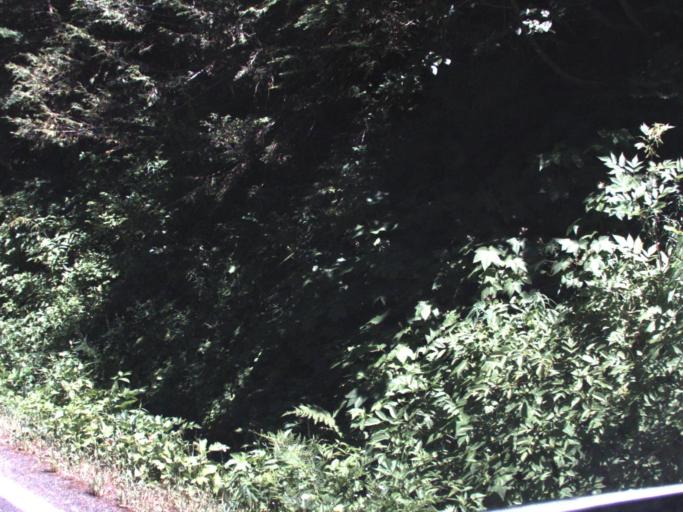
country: US
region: Washington
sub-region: King County
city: Enumclaw
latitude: 46.8483
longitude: -121.5253
